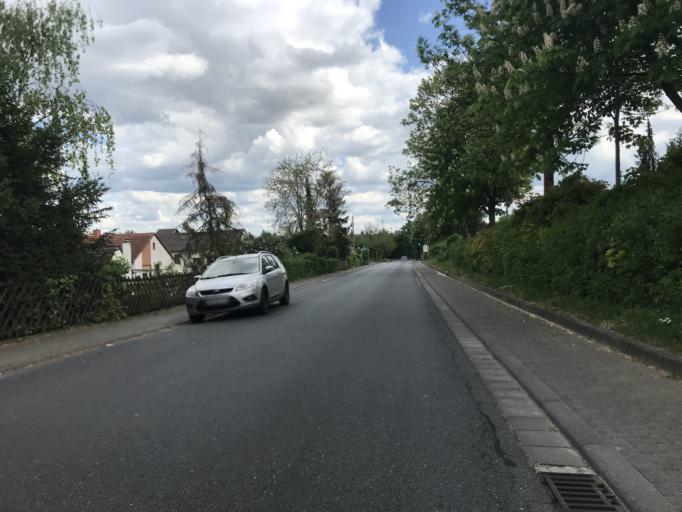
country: DE
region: Rheinland-Pfalz
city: Gau-Bischofsheim
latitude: 49.9117
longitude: 8.2755
